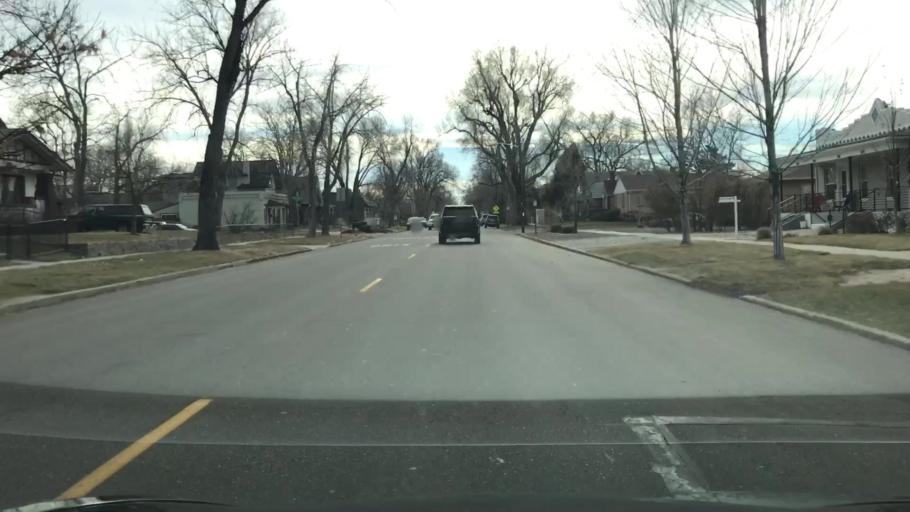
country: US
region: Colorado
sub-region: Arapahoe County
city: Englewood
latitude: 39.6919
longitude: -104.9828
